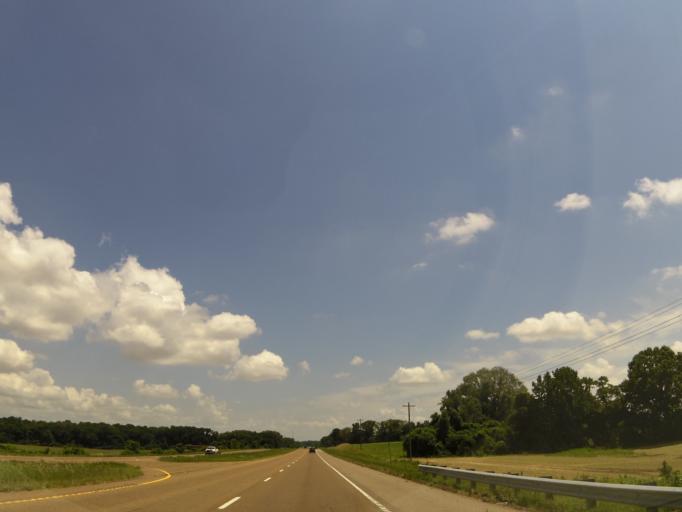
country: US
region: Tennessee
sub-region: Lauderdale County
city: Halls
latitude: 35.9332
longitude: -89.2896
